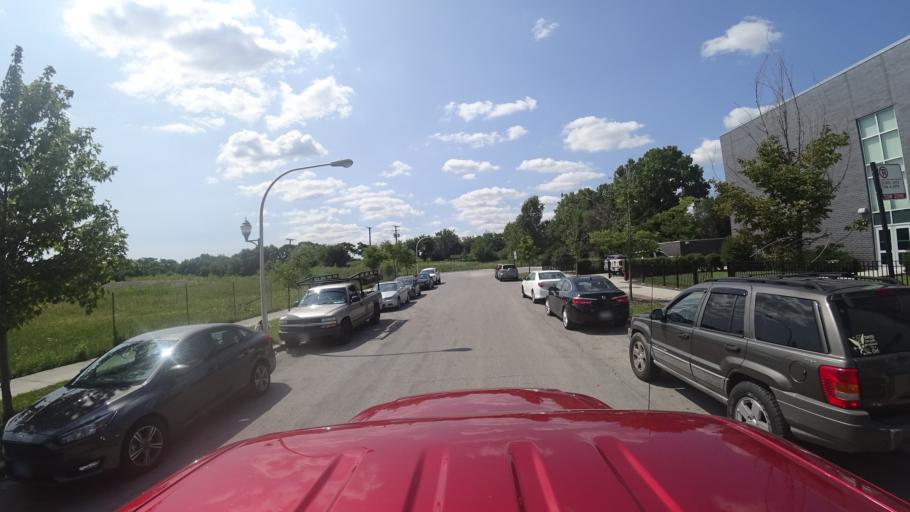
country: US
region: Illinois
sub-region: Cook County
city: Chicago
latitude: 41.8062
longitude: -87.6893
